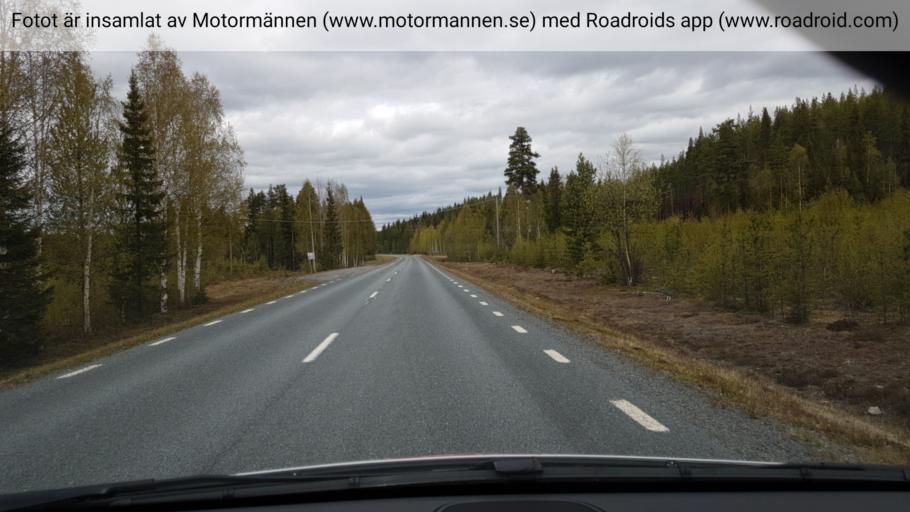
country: SE
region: Vaesterbotten
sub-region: Mala Kommun
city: Mala
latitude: 65.0642
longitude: 18.3729
